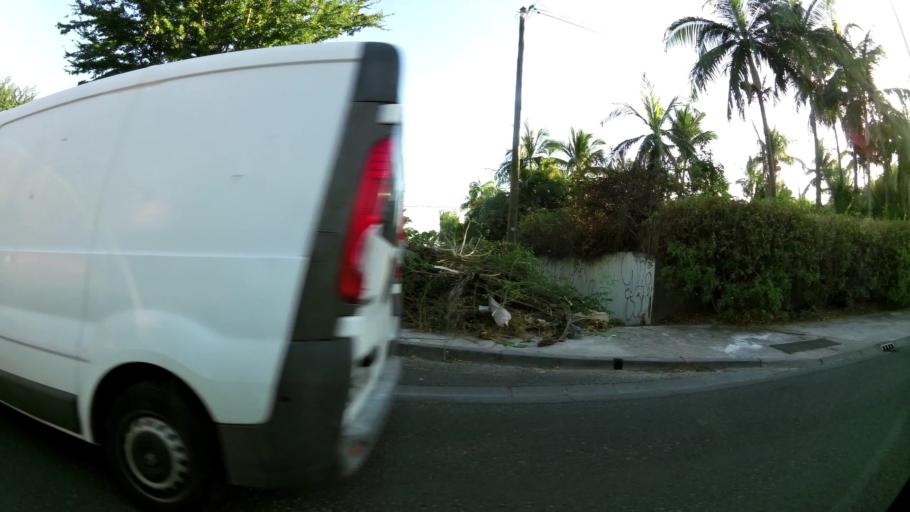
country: RE
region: Reunion
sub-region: Reunion
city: Trois-Bassins
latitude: -21.0999
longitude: 55.2434
